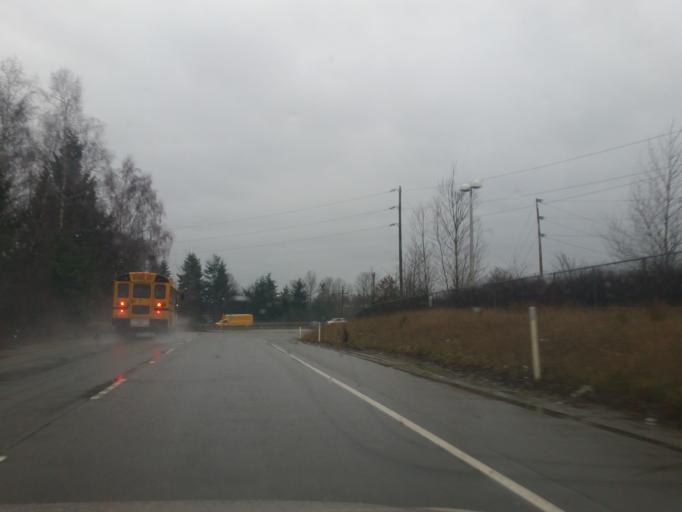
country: US
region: Washington
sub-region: Snohomish County
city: Mukilteo
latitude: 47.9238
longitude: -122.2611
